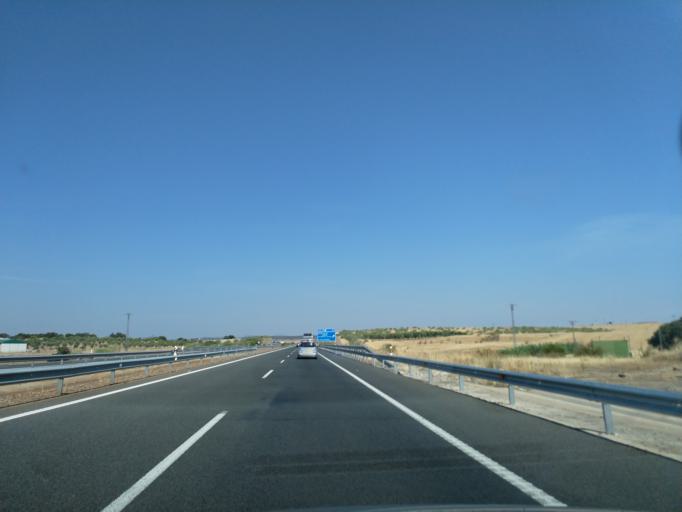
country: ES
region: Extremadura
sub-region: Provincia de Badajoz
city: Aljucen
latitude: 39.0240
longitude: -6.3323
